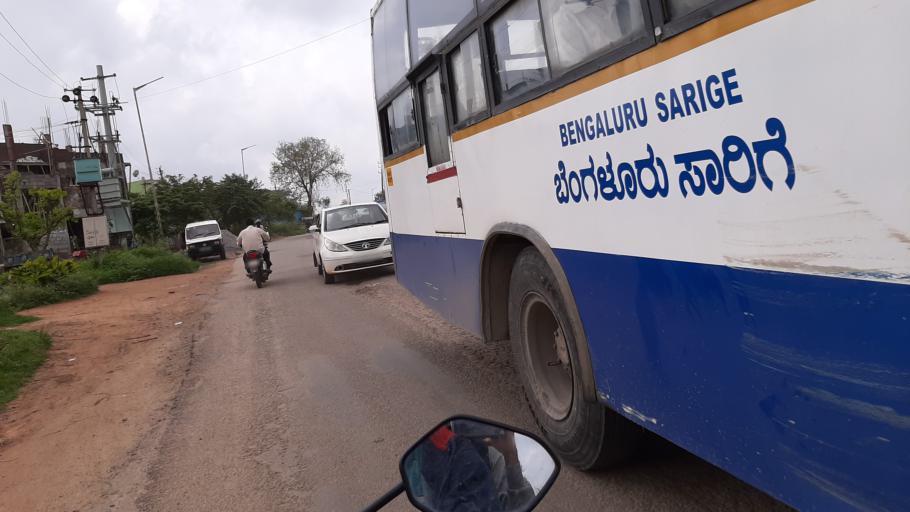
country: IN
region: Karnataka
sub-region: Ramanagara
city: Magadi
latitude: 12.9494
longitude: 77.2380
